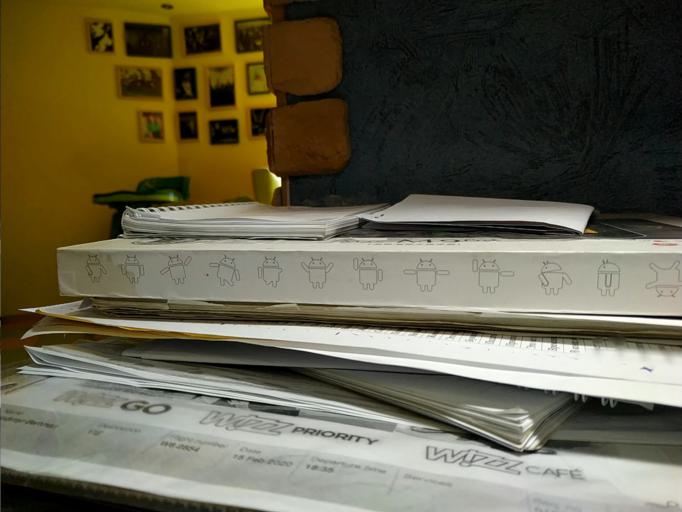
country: RU
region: Novgorod
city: Utorgosh
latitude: 58.2556
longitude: 29.8942
